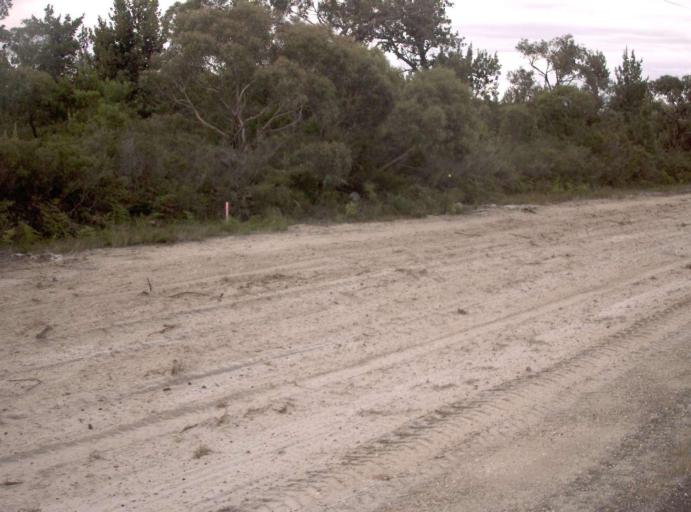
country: AU
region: Victoria
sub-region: East Gippsland
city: Bairnsdale
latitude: -38.0828
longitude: 147.5301
